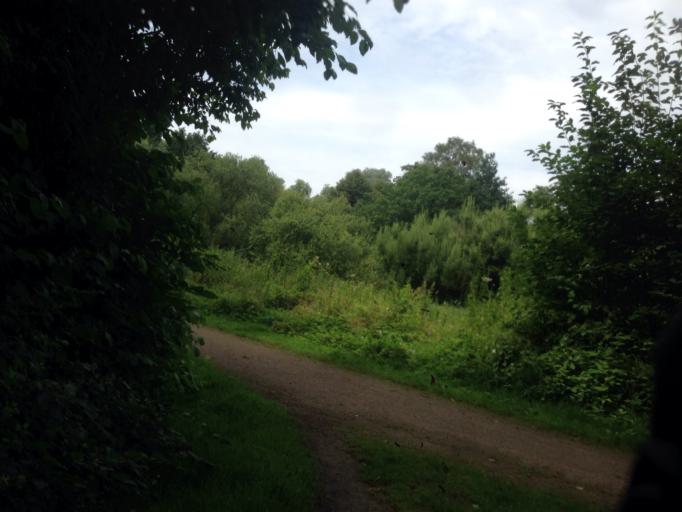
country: DE
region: Hamburg
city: Farmsen-Berne
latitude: 53.5926
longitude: 10.1244
